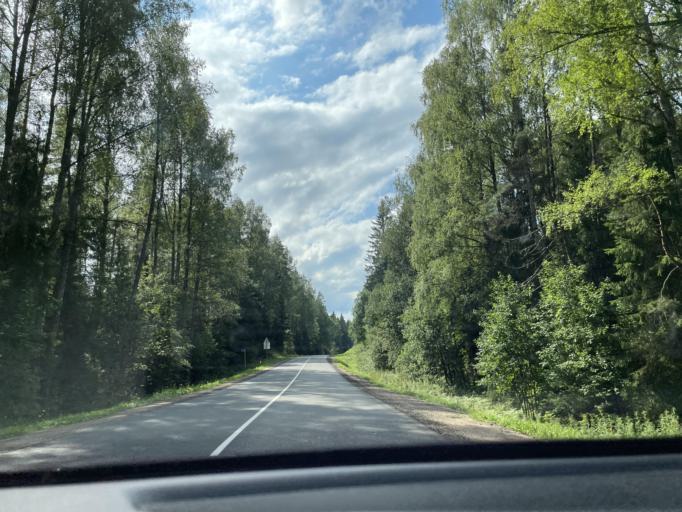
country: RU
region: Novgorod
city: Valday
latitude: 58.0325
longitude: 33.2144
